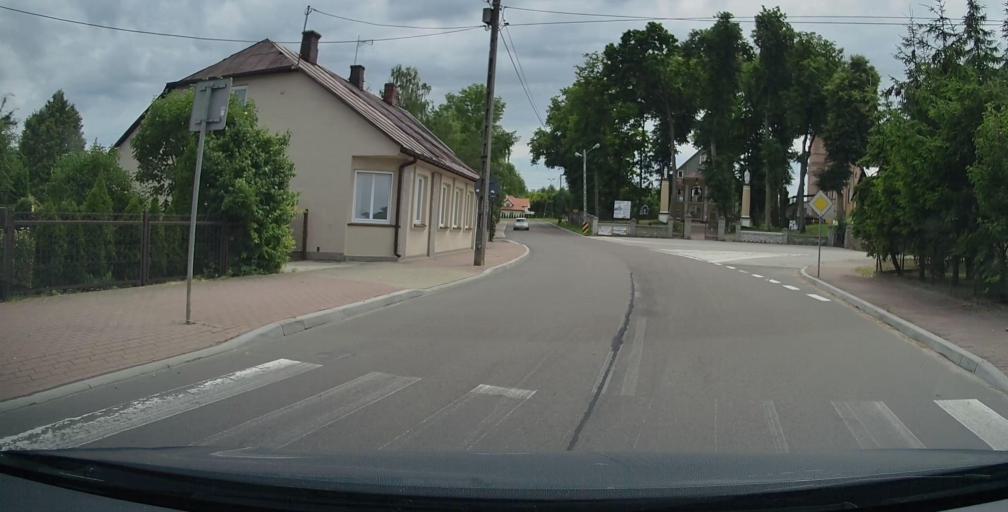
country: PL
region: Masovian Voivodeship
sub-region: Powiat losicki
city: Sarnaki
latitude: 52.3139
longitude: 22.8909
